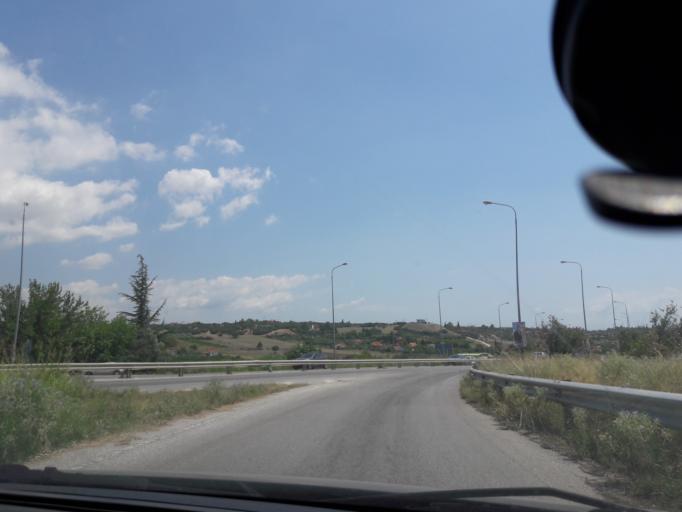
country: GR
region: Central Macedonia
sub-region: Nomos Chalkidikis
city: Nea Kallikrateia
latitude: 40.3167
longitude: 23.0911
